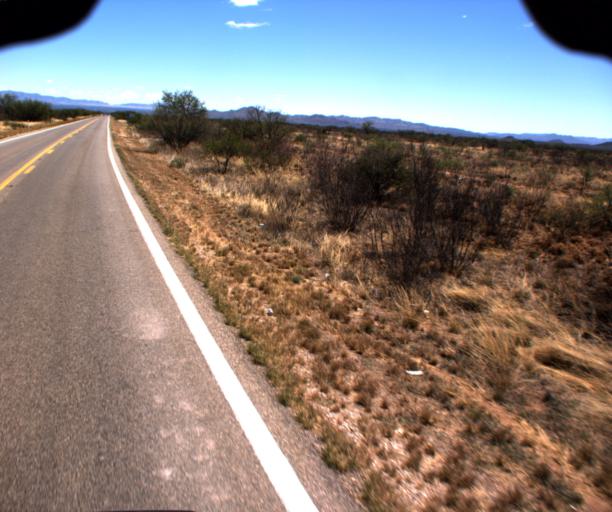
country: US
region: Arizona
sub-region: Cochise County
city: Huachuca City
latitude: 31.7083
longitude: -110.2809
